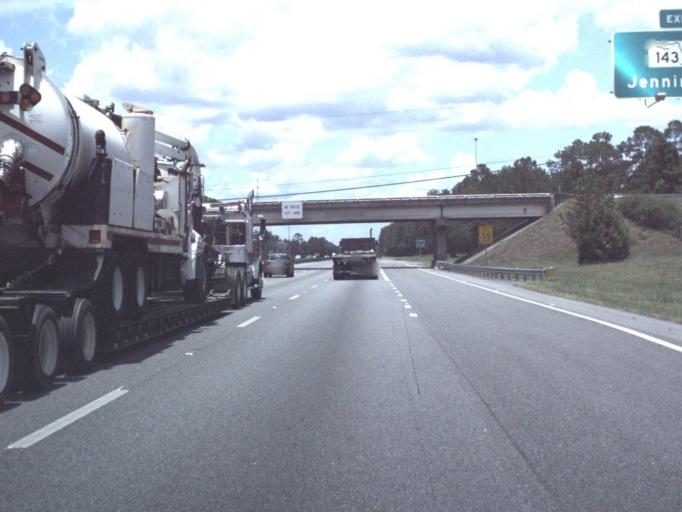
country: US
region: Georgia
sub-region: Echols County
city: Statenville
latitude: 30.5938
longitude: -83.1189
